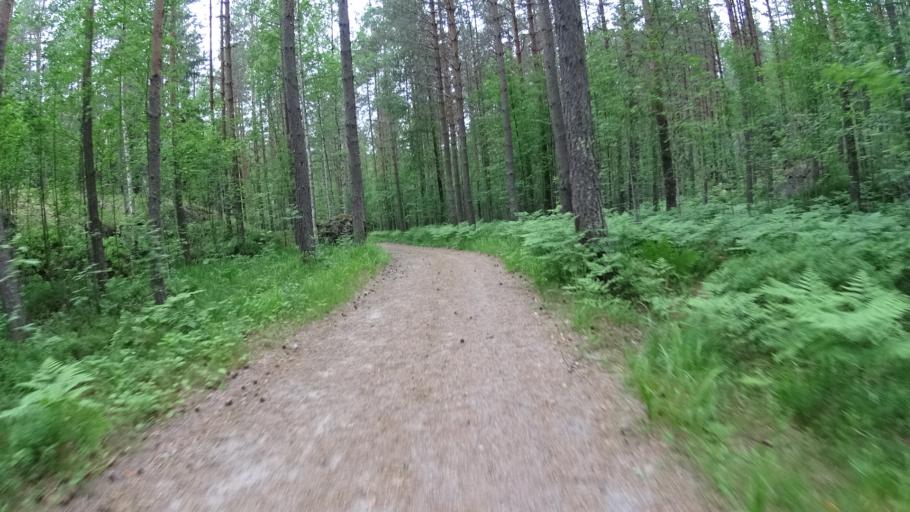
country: FI
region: Uusimaa
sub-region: Helsinki
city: Espoo
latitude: 60.2943
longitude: 24.5796
